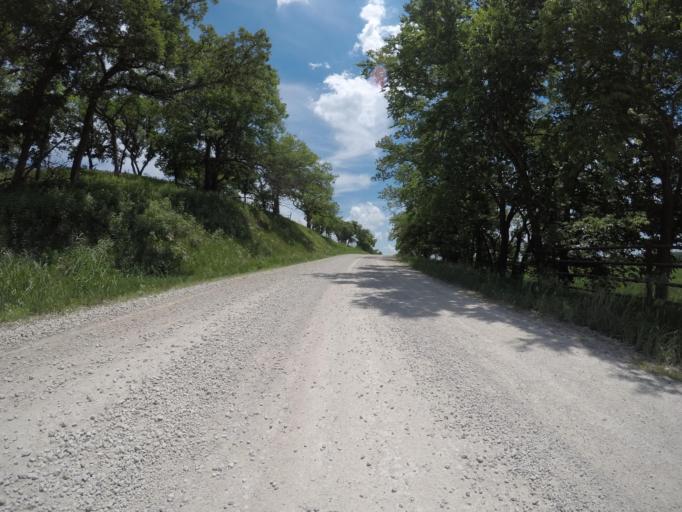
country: US
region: Kansas
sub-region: Wabaunsee County
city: Alma
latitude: 38.8992
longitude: -96.2069
